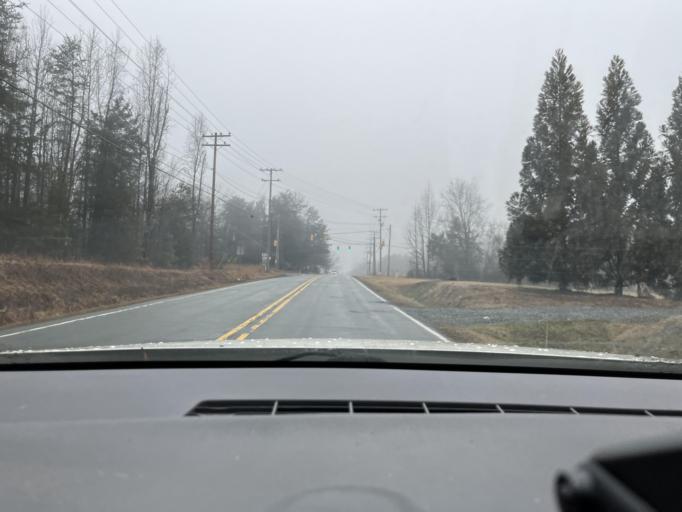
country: US
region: North Carolina
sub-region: Guilford County
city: Pleasant Garden
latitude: 35.9899
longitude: -79.7778
